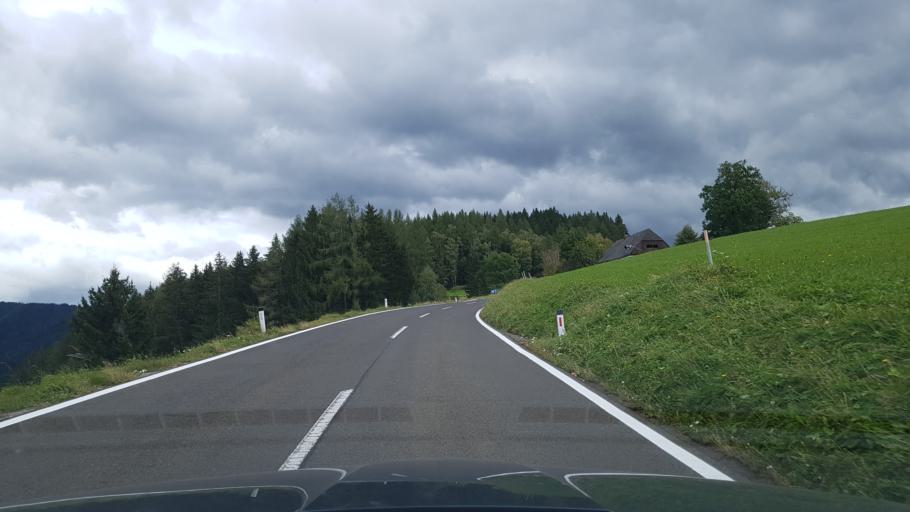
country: AT
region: Styria
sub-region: Politischer Bezirk Murtal
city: Kleinlobming
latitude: 47.1388
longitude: 14.8412
